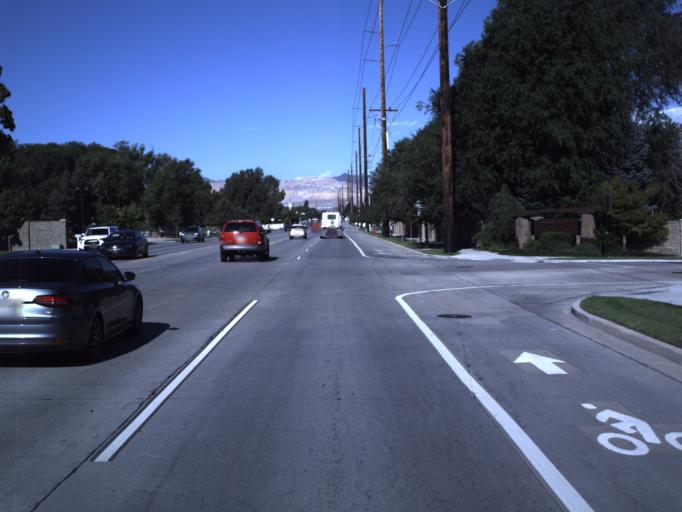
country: US
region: Utah
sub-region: Salt Lake County
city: South Jordan Heights
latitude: 40.5442
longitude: -111.9417
